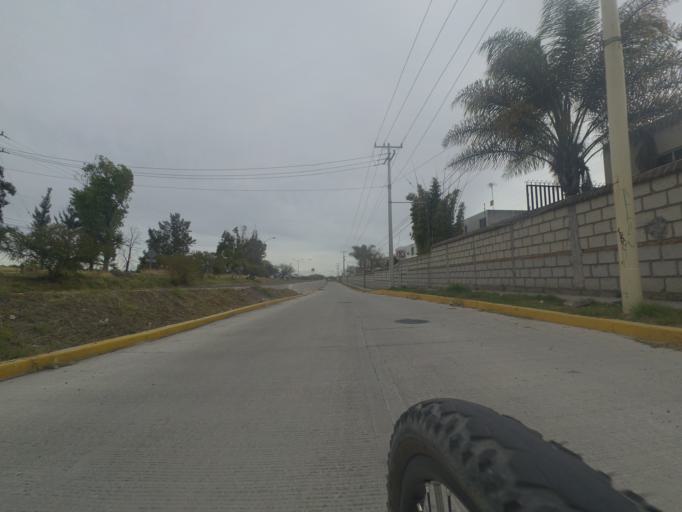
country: MX
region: Aguascalientes
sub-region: Aguascalientes
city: La Loma de los Negritos
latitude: 21.8502
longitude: -102.3536
